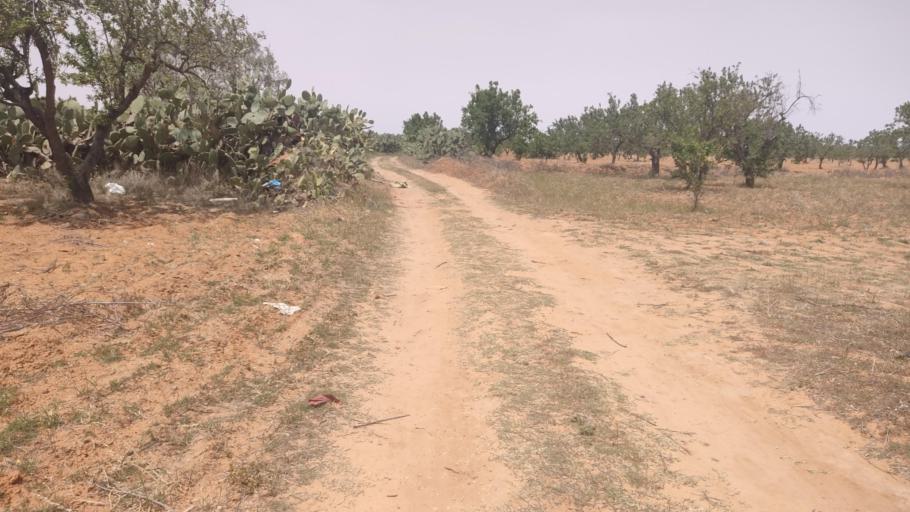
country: TN
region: Safaqis
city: Sfax
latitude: 34.8479
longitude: 10.5948
